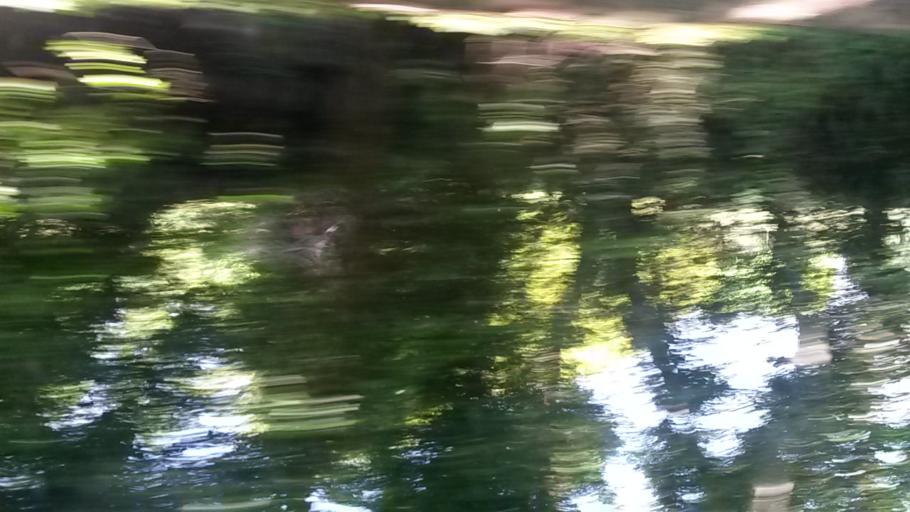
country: IE
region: Leinster
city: Donabate
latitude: 53.4899
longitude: -6.1698
